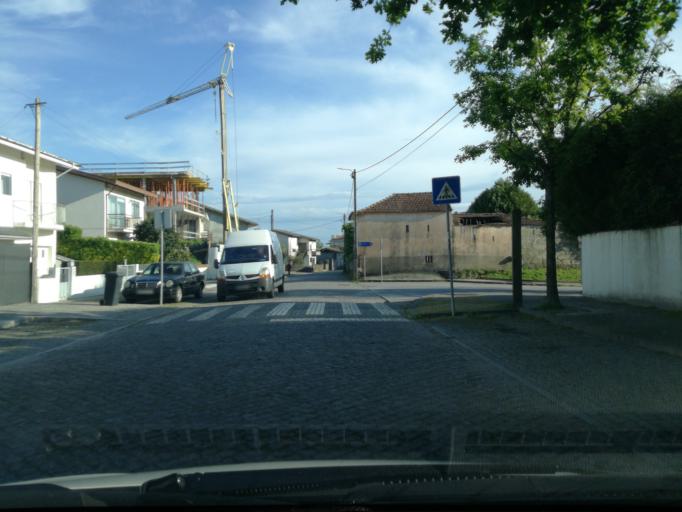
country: PT
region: Porto
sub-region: Maia
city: Gemunde
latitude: 41.2522
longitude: -8.6482
